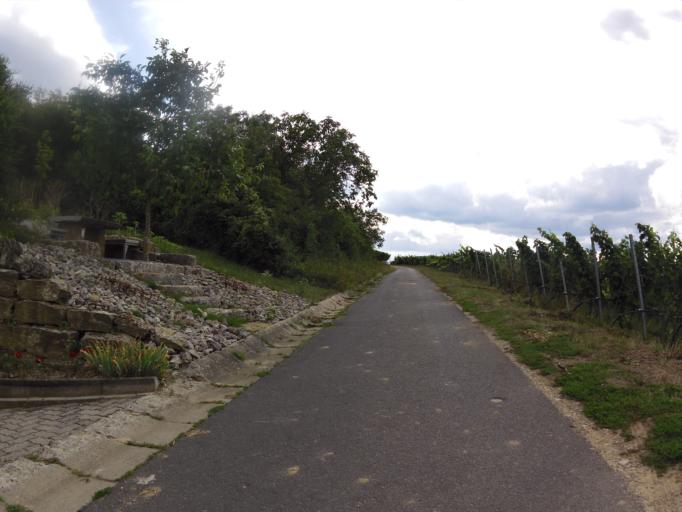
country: DE
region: Bavaria
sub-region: Regierungsbezirk Unterfranken
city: Sommerhausen
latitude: 49.6965
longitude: 10.0351
